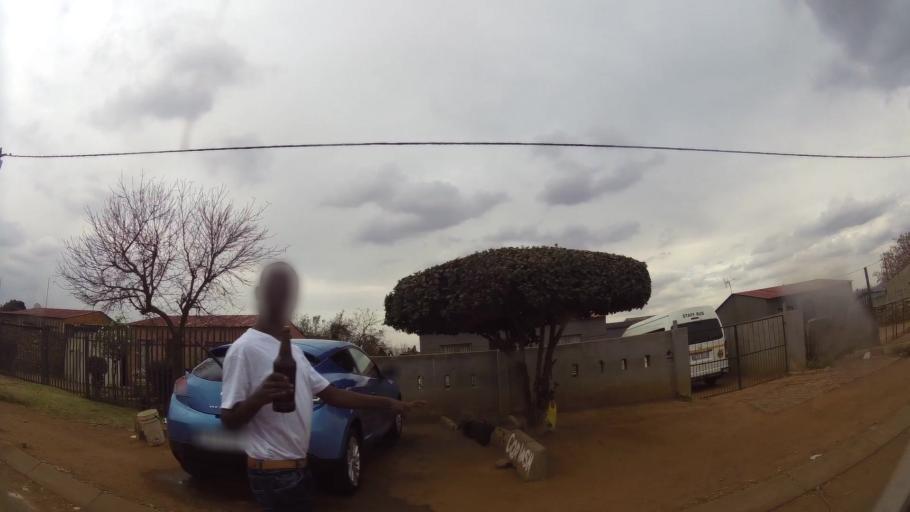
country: ZA
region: Gauteng
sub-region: Ekurhuleni Metropolitan Municipality
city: Germiston
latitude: -26.3998
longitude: 28.1371
